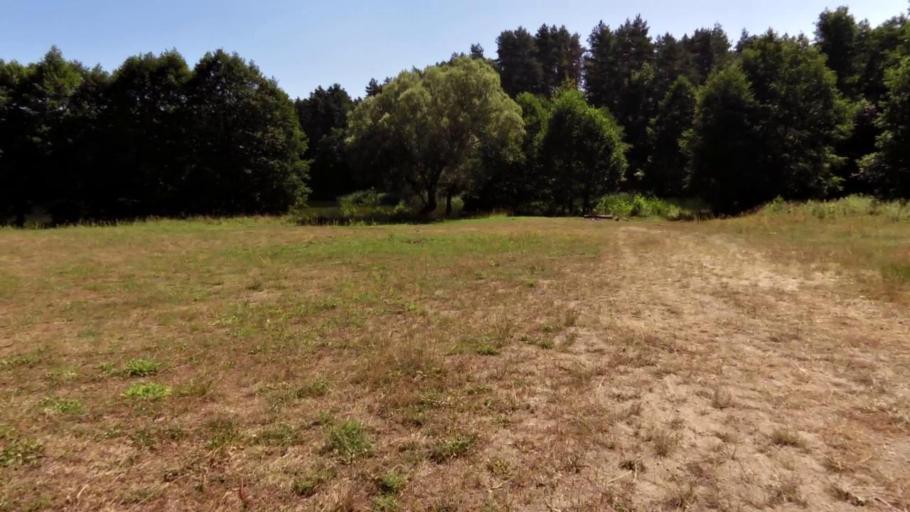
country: PL
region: West Pomeranian Voivodeship
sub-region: Powiat szczecinecki
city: Szczecinek
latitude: 53.6005
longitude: 16.6658
